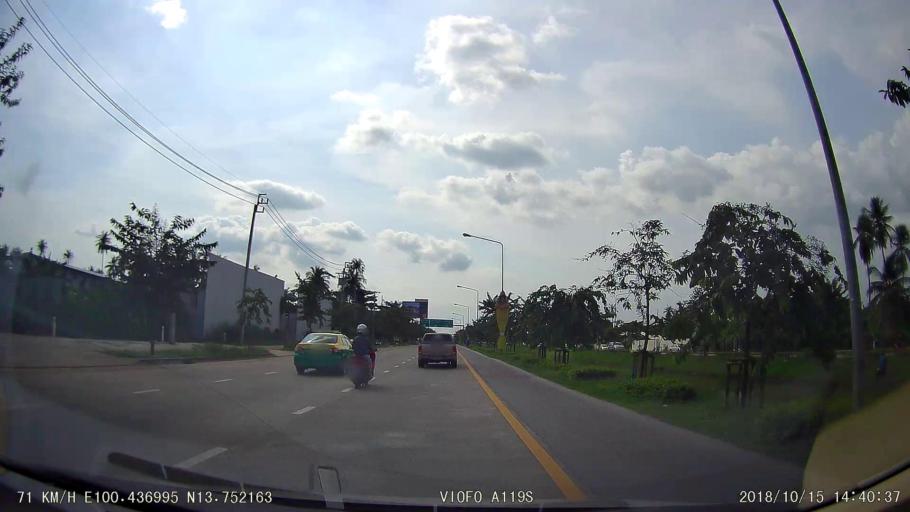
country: TH
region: Bangkok
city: Taling Chan
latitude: 13.7522
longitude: 100.4368
